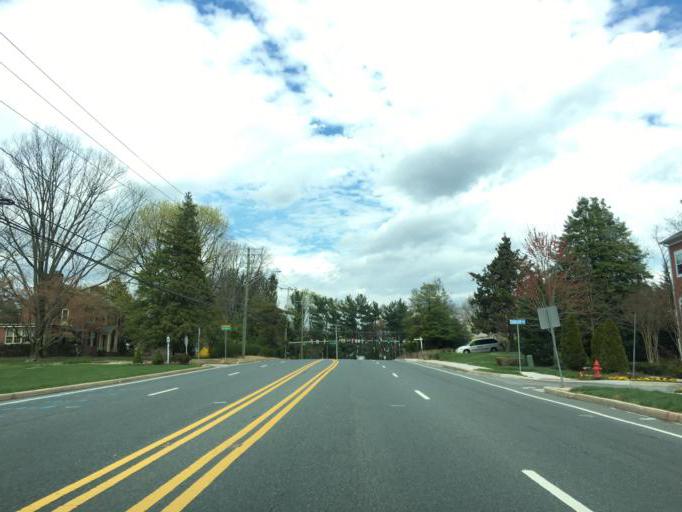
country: US
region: Maryland
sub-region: Baltimore County
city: Towson
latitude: 39.3811
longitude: -76.6273
